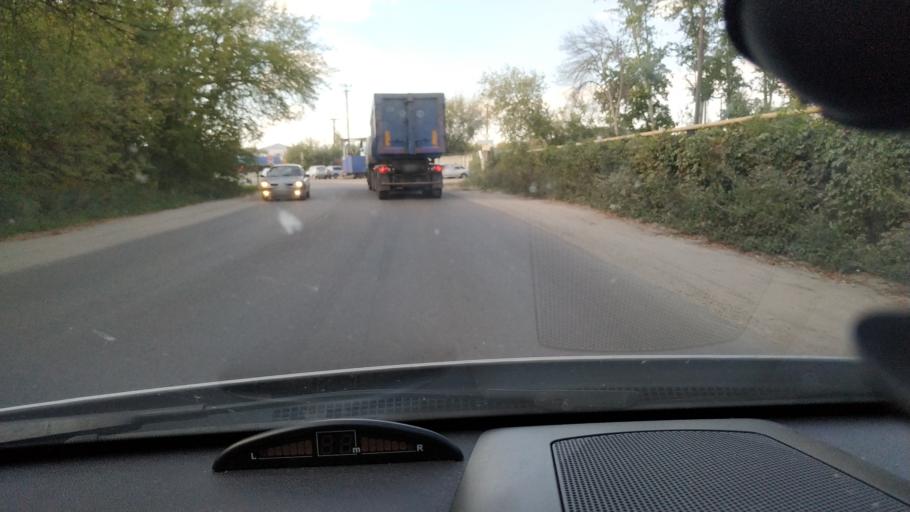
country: RU
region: Rjazan
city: Ryazan'
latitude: 54.6638
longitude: 39.6276
